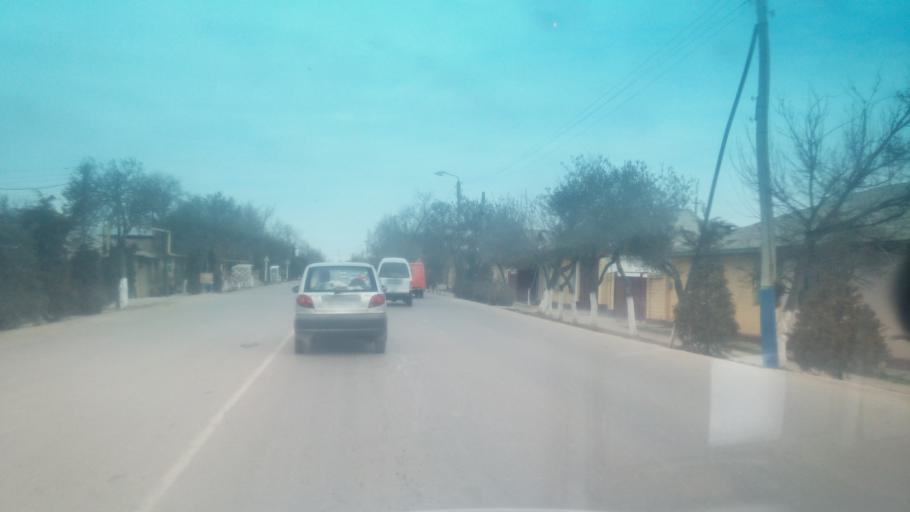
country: UZ
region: Sirdaryo
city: Guliston
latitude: 40.4786
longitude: 68.7808
